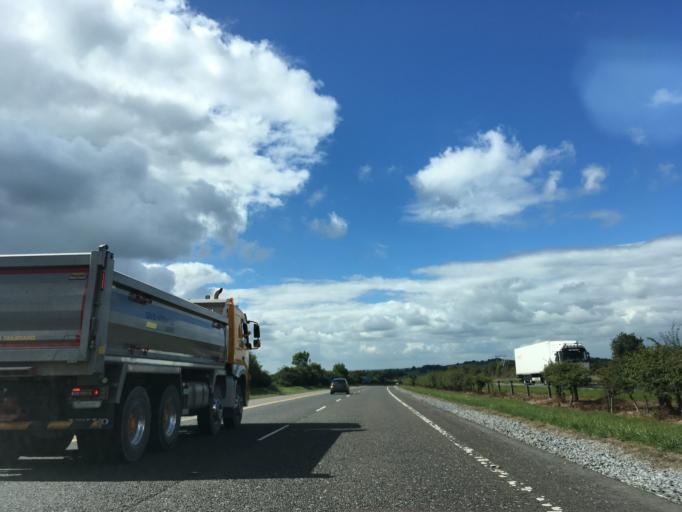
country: IE
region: Munster
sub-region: County Cork
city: Watergrasshill
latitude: 52.0032
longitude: -8.3453
